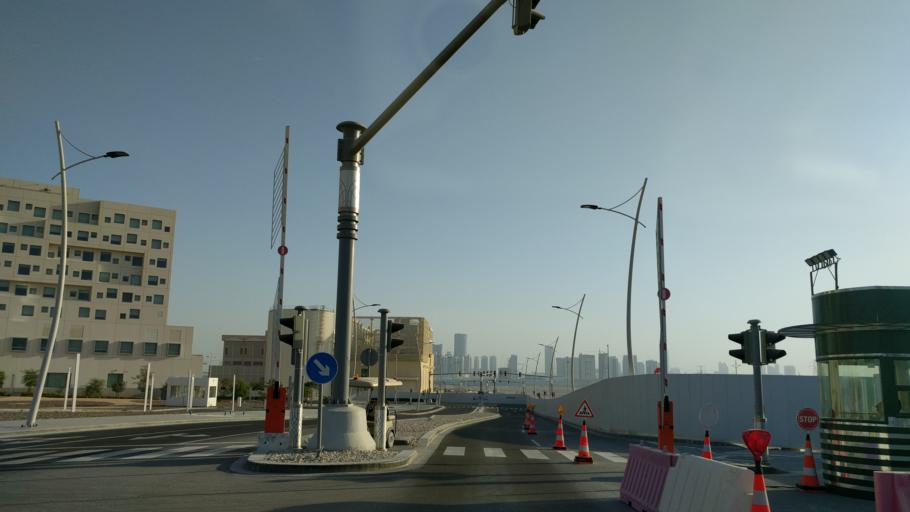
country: AE
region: Abu Dhabi
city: Abu Dhabi
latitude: 24.5263
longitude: 54.4327
